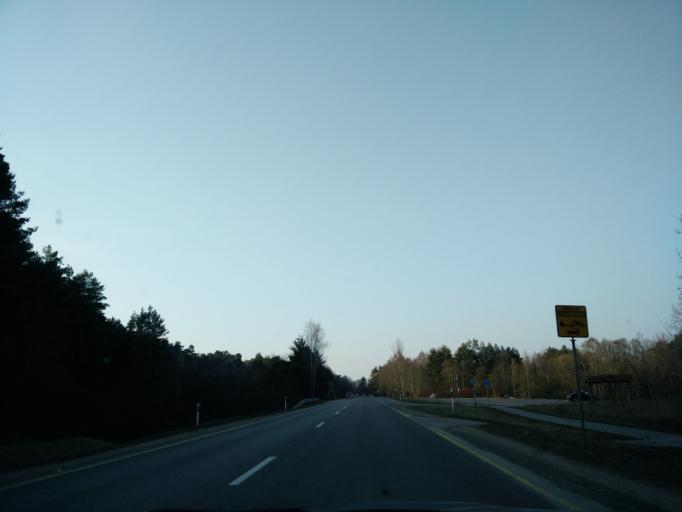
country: LT
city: Trakai
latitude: 54.6573
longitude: 24.9163
